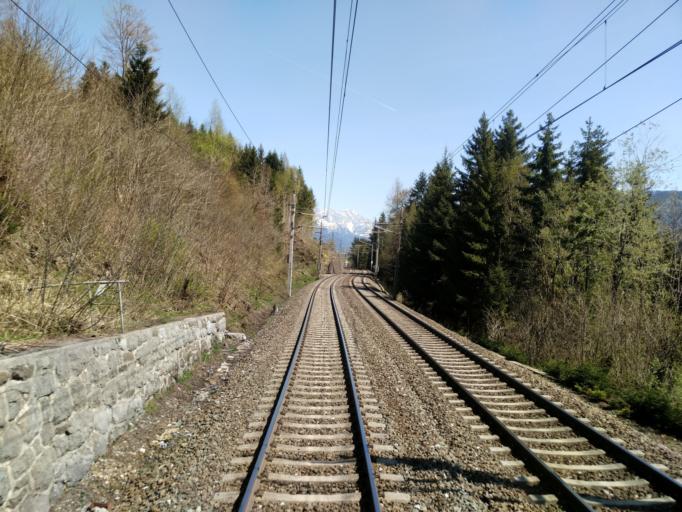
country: AT
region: Salzburg
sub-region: Politischer Bezirk Zell am See
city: Leogang
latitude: 47.4426
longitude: 12.7122
